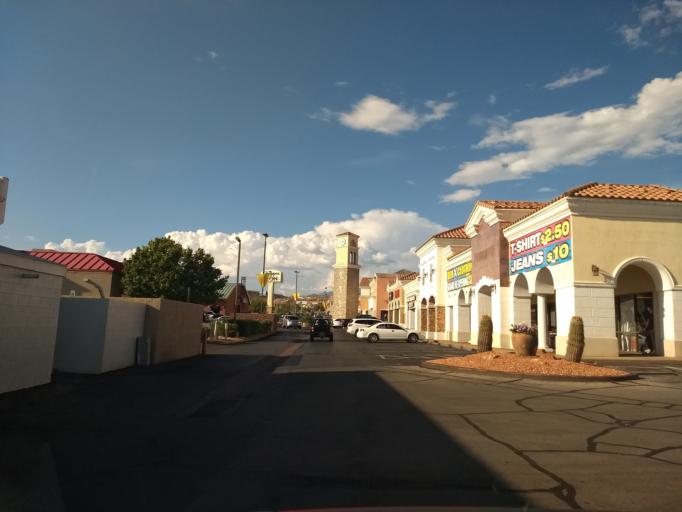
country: US
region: Utah
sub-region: Washington County
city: Saint George
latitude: 37.1101
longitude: -113.5537
